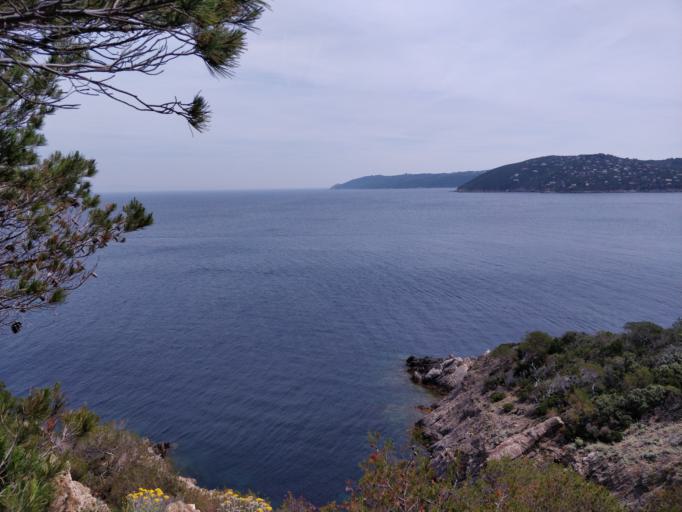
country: FR
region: Provence-Alpes-Cote d'Azur
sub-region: Departement du Var
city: Le Lavandou
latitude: 43.0165
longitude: 6.4124
